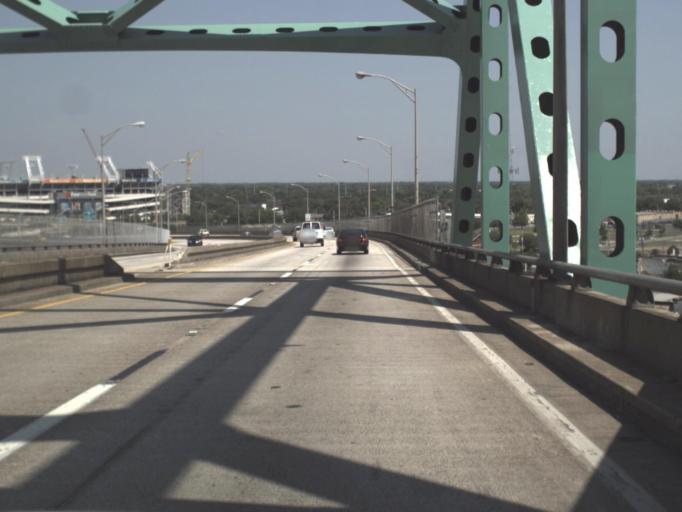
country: US
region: Florida
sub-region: Duval County
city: Jacksonville
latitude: 30.3184
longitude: -81.6294
